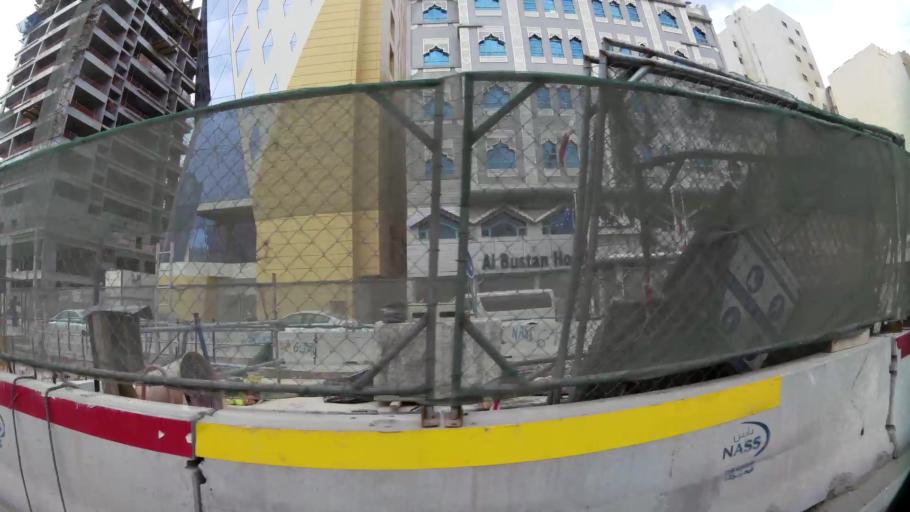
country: QA
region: Baladiyat ad Dawhah
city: Doha
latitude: 25.2868
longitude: 51.5456
